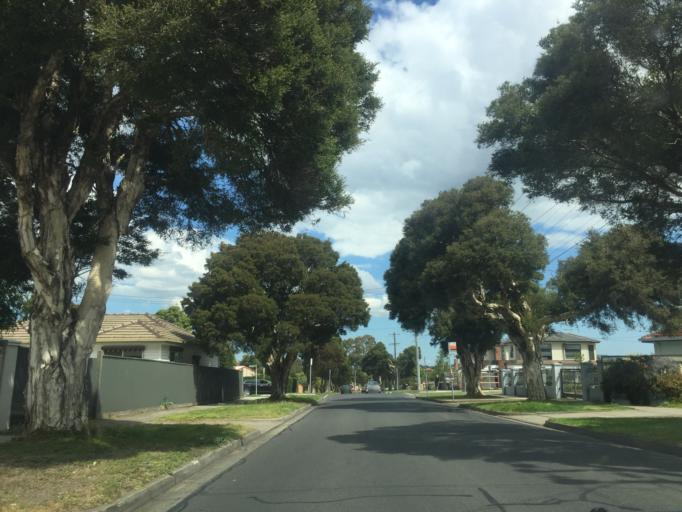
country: AU
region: Victoria
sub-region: Darebin
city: Kingsbury
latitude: -37.7065
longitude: 145.0202
